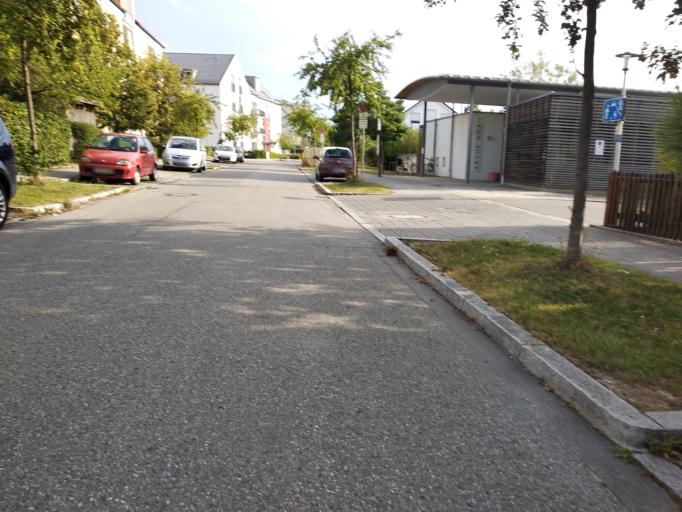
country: DE
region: Bavaria
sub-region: Upper Bavaria
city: Neubiberg
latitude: 48.0860
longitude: 11.6596
